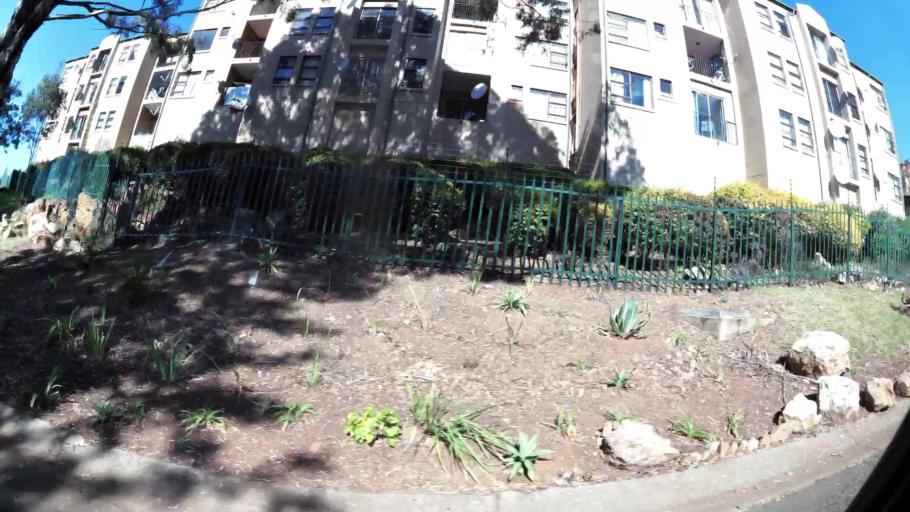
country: ZA
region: Gauteng
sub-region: City of Johannesburg Metropolitan Municipality
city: Roodepoort
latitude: -26.1169
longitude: 27.8567
